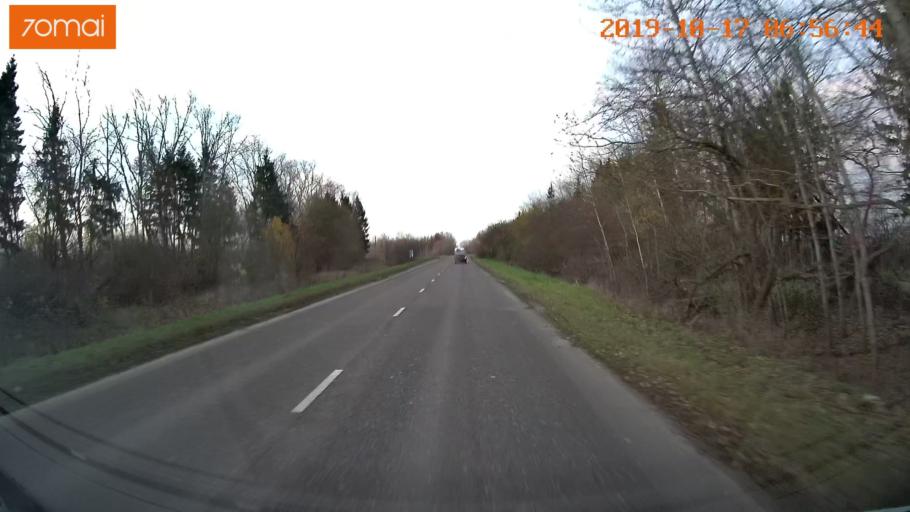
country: RU
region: Vladimir
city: Suzdal'
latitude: 56.4432
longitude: 40.4449
